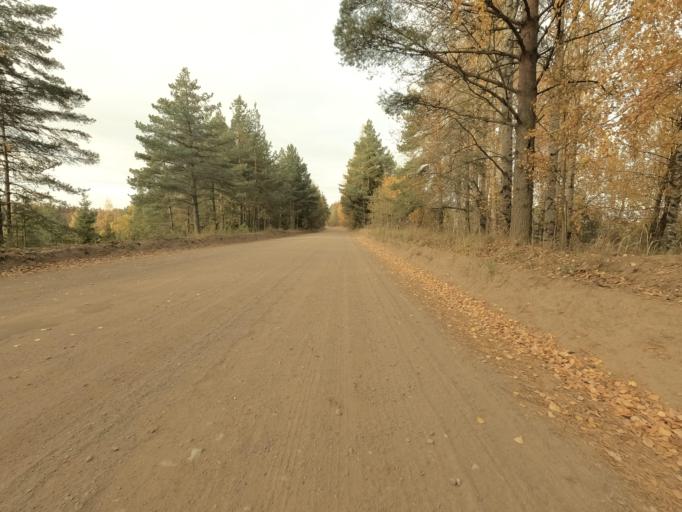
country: RU
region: Leningrad
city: Priladozhskiy
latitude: 59.6753
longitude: 31.3661
